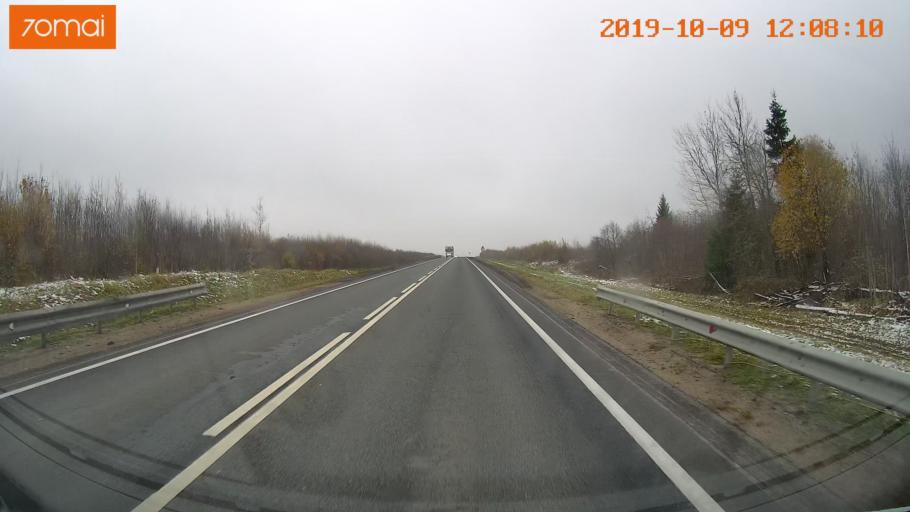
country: RU
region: Jaroslavl
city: Prechistoye
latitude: 58.5902
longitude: 40.3459
